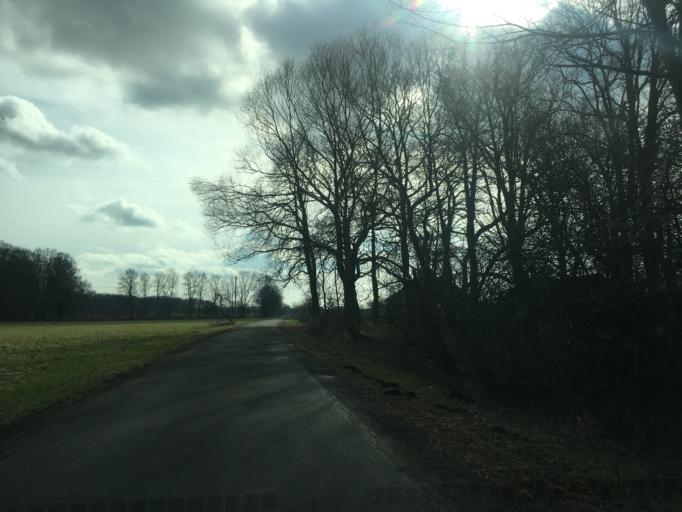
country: DE
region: North Rhine-Westphalia
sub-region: Regierungsbezirk Munster
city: Greven
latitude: 52.0386
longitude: 7.6468
